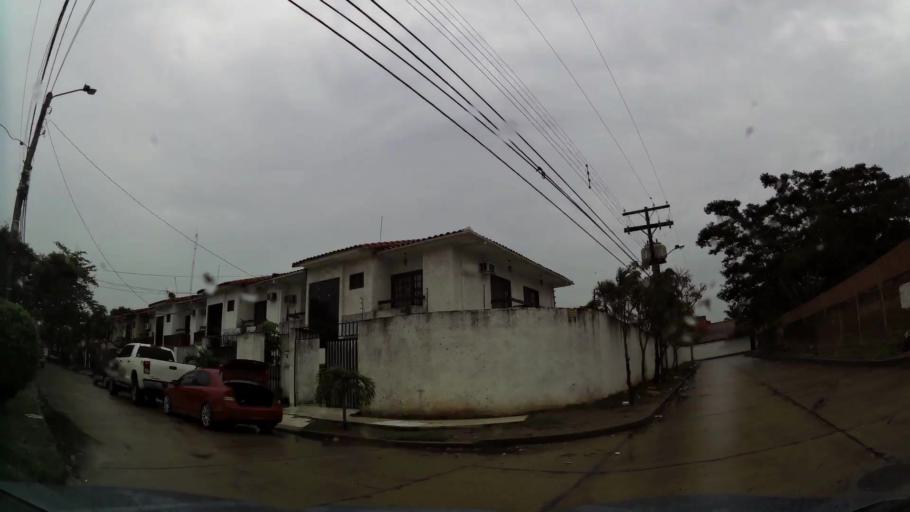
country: BO
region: Santa Cruz
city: Santa Cruz de la Sierra
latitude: -17.7866
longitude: -63.2086
